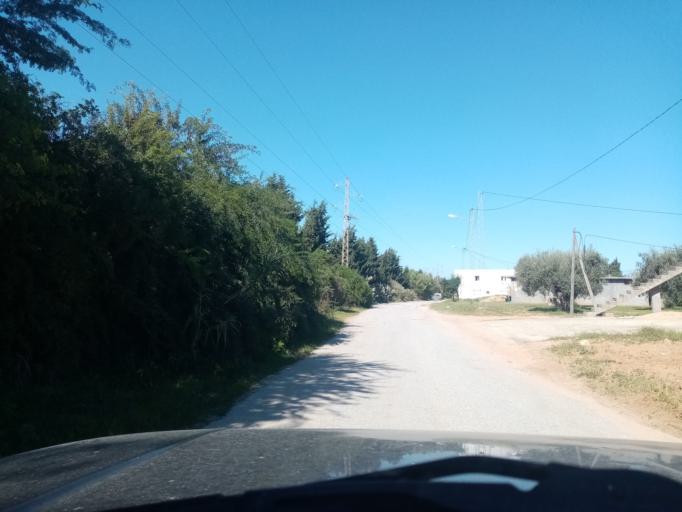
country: TN
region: Nabul
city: Bu `Urqub
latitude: 36.5692
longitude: 10.5779
